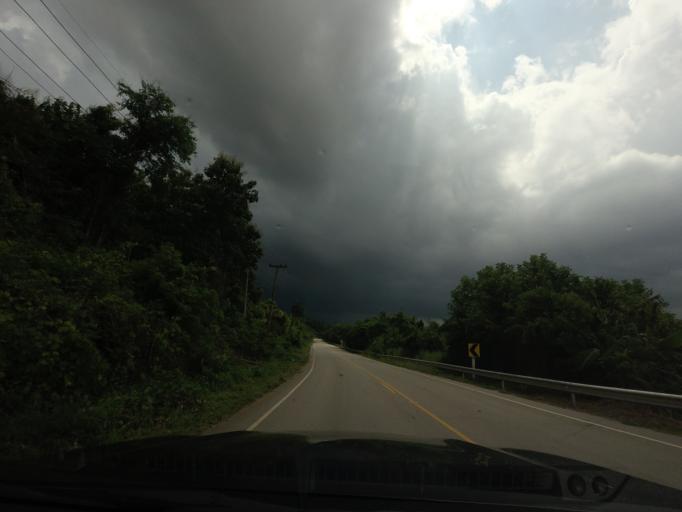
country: LA
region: Vientiane
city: Muang Sanakham
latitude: 17.9760
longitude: 101.7472
